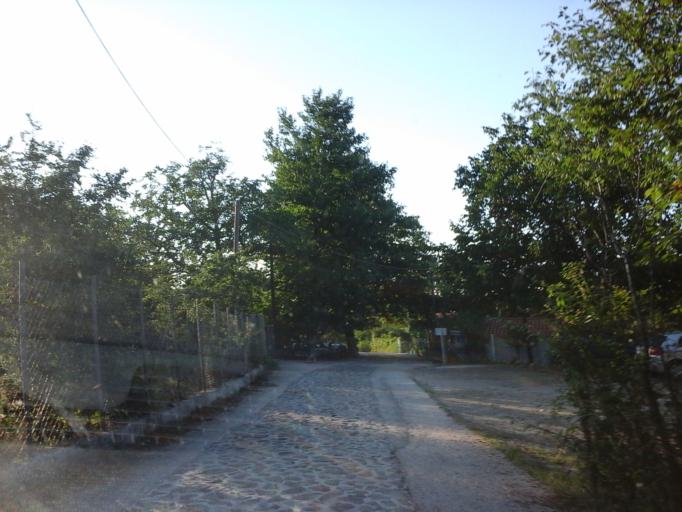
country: GR
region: East Macedonia and Thrace
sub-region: Nomos Evrou
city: Samothraki
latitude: 40.4937
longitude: 25.6116
